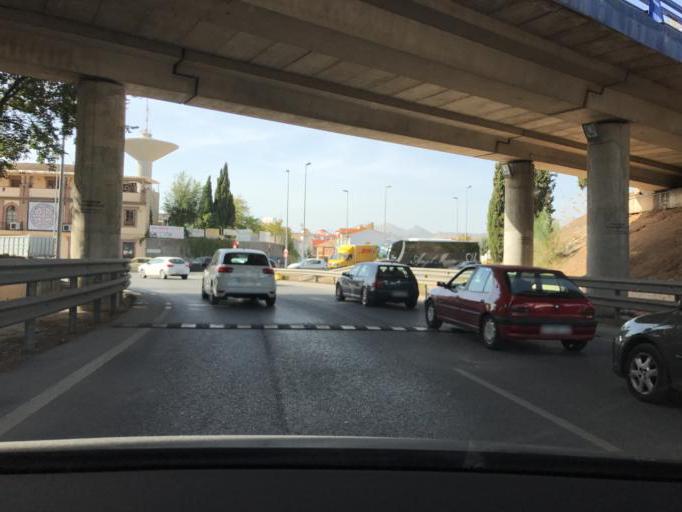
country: ES
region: Andalusia
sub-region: Provincia de Granada
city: Maracena
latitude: 37.2106
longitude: -3.6234
